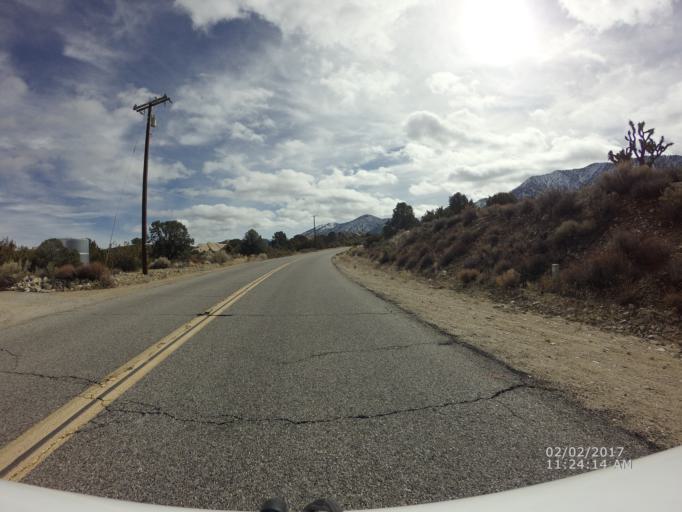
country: US
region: California
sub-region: Los Angeles County
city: Littlerock
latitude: 34.4293
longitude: -117.8718
